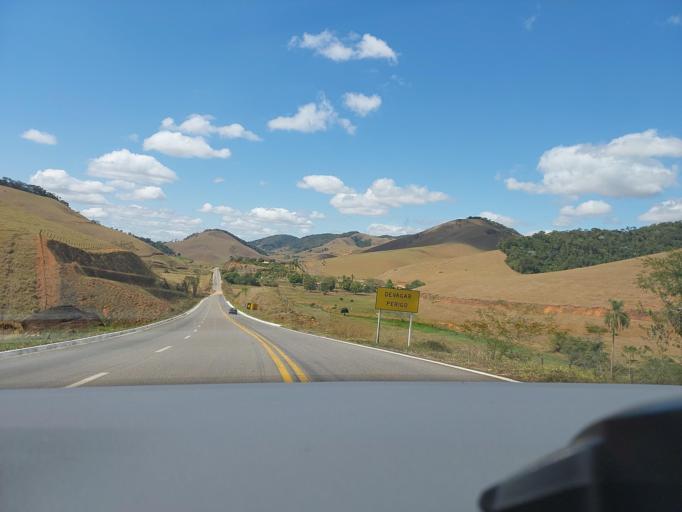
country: BR
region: Minas Gerais
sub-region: Mirai
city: Mirai
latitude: -21.0489
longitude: -42.5225
